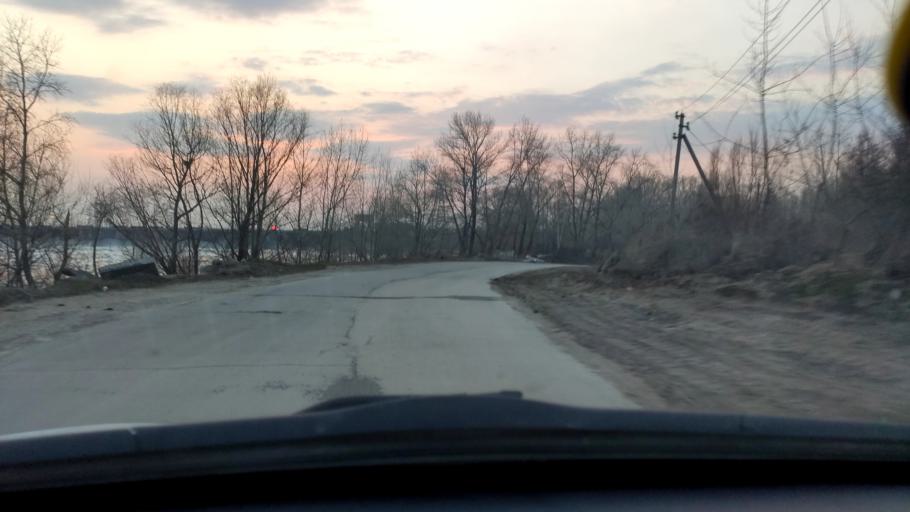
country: RU
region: Samara
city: Zhigulevsk
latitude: 53.4577
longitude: 49.5136
